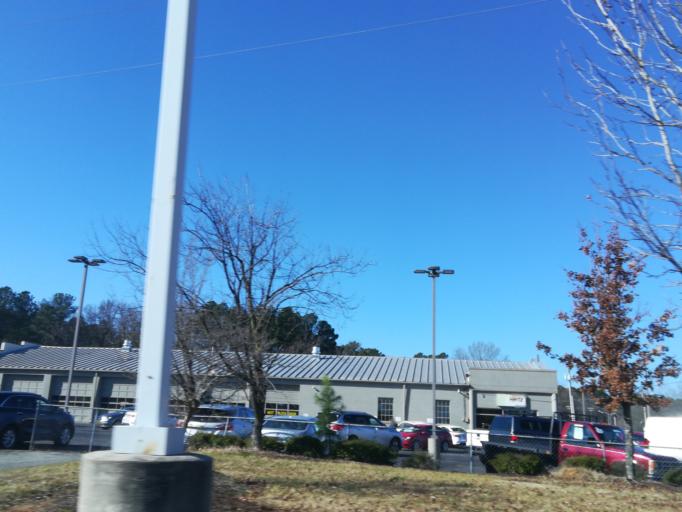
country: US
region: North Carolina
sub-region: Durham County
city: Durham
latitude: 36.0222
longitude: -78.9538
